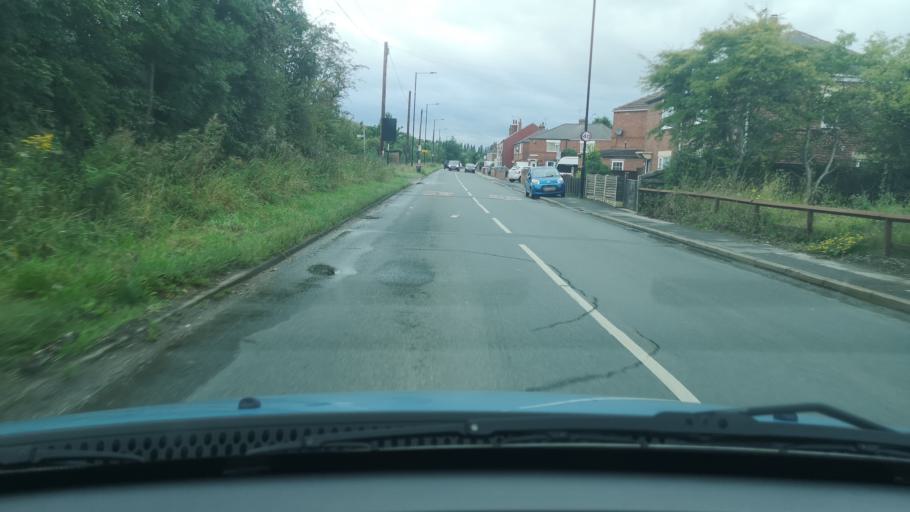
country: GB
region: England
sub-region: Doncaster
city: Hatfield
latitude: 53.5997
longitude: -1.0063
